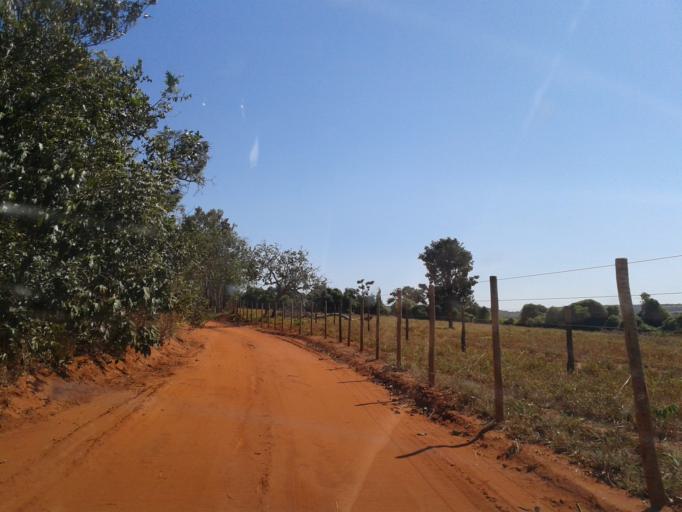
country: BR
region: Minas Gerais
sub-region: Monte Alegre De Minas
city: Monte Alegre de Minas
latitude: -18.8786
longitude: -49.1306
